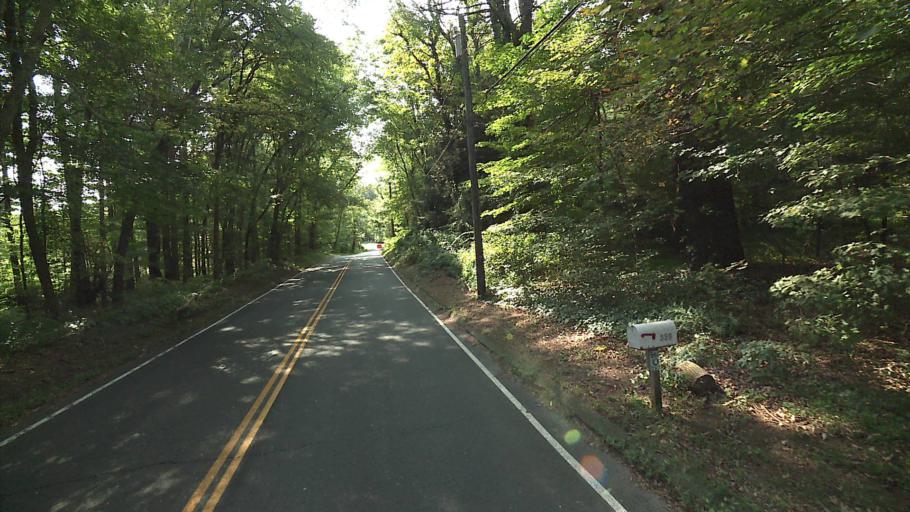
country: US
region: Connecticut
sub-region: Fairfield County
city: Westport
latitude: 41.2310
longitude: -73.3197
